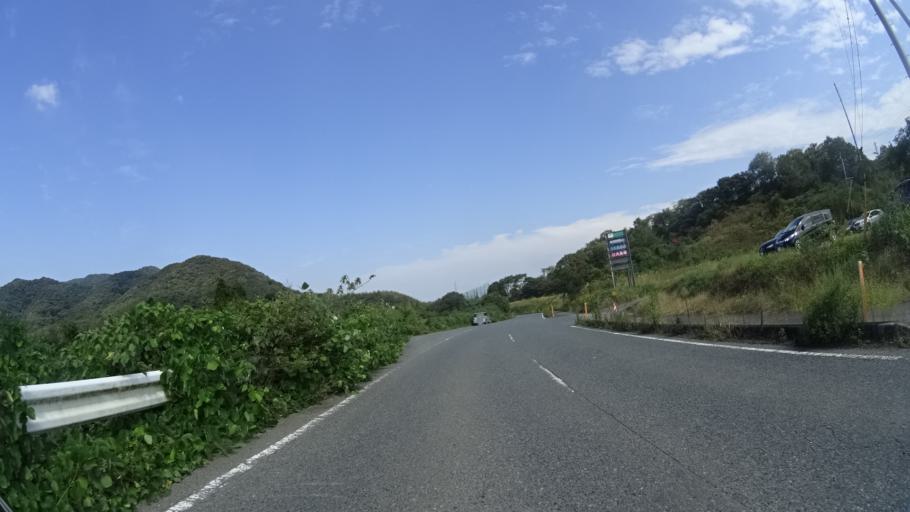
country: JP
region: Kumamoto
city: Uto
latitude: 32.6721
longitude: 130.7200
